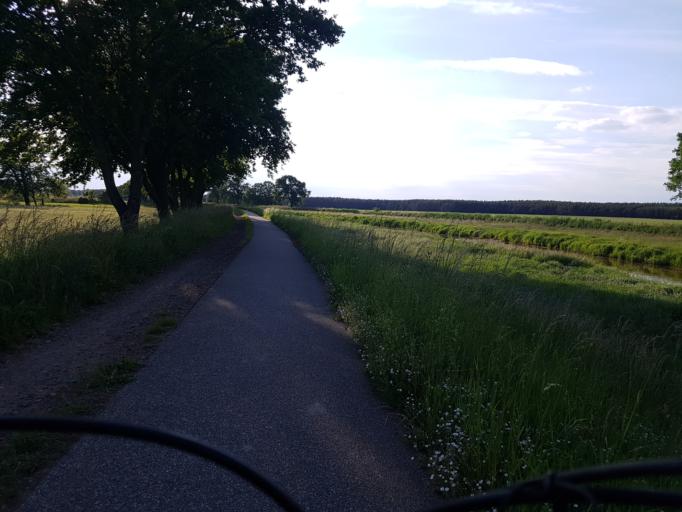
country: DE
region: Brandenburg
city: Elsterwerda
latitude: 51.4787
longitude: 13.4614
